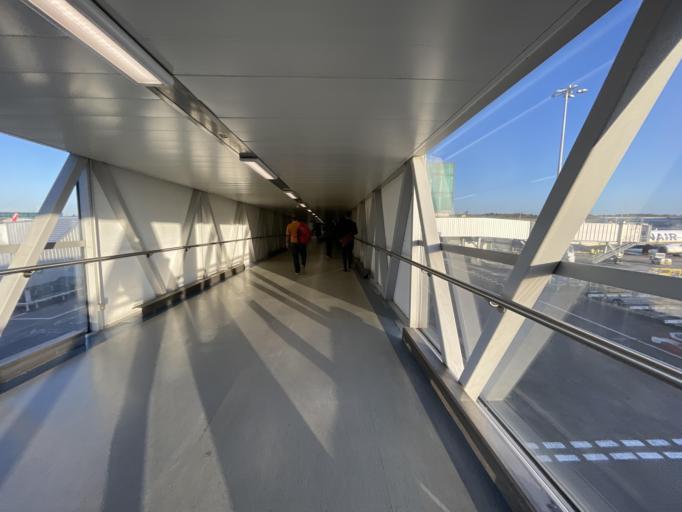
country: GB
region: England
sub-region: Essex
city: Takeley
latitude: 51.8903
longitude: 0.2584
